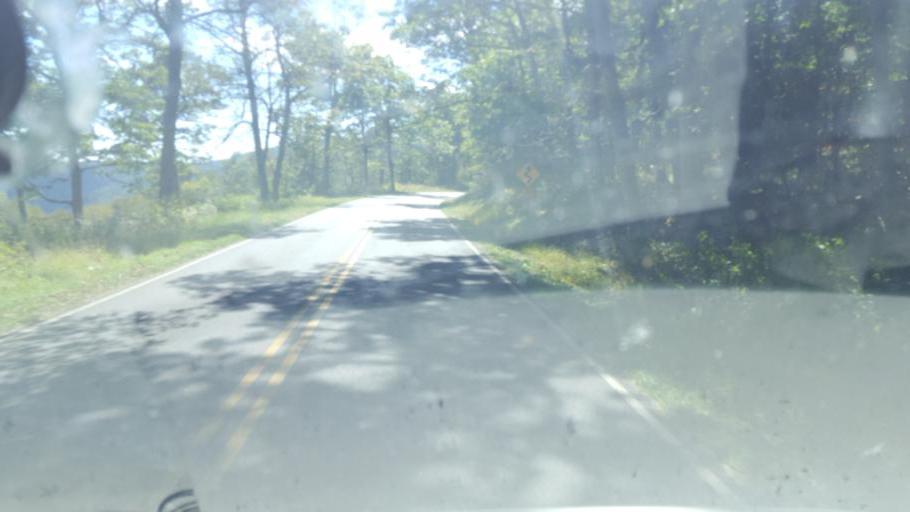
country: US
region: Virginia
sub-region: Greene County
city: Stanardsville
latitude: 38.3886
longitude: -78.5081
